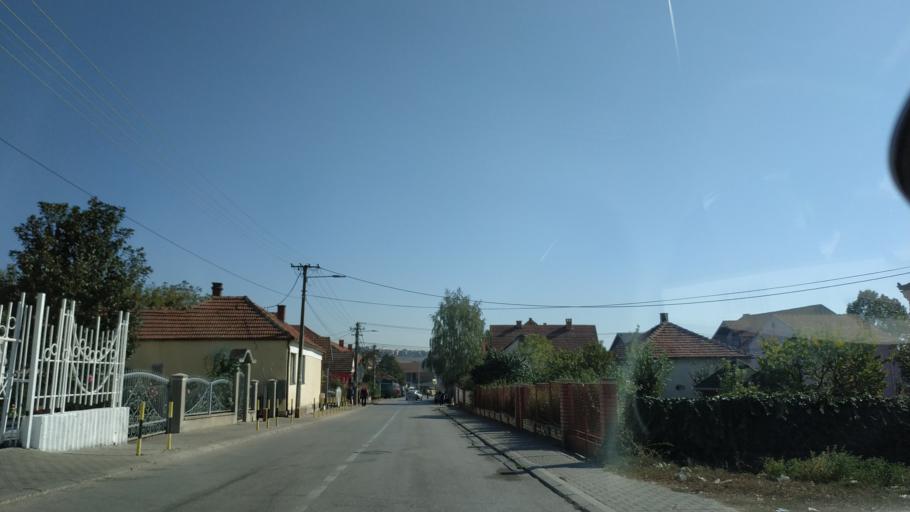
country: RS
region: Central Serbia
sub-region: Nisavski Okrug
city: Aleksinac
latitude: 43.5402
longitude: 21.6986
